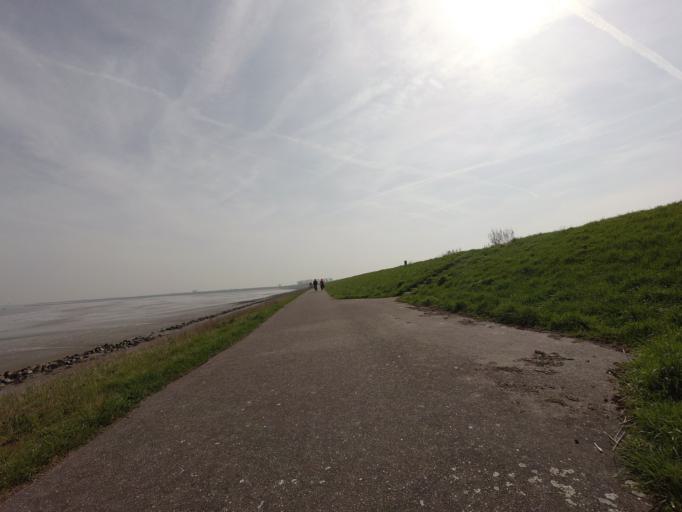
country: NL
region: Zeeland
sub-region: Gemeente Hulst
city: Hulst
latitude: 51.3754
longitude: 4.0405
